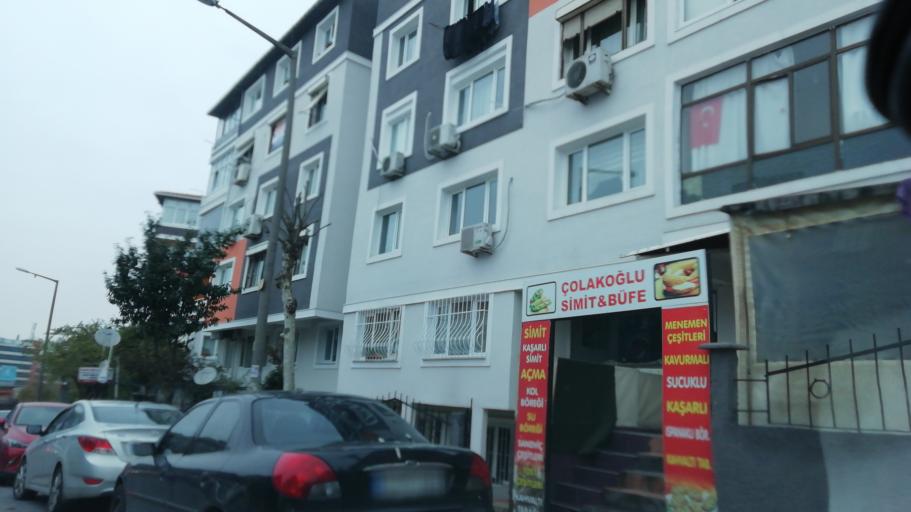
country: TR
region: Istanbul
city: Mahmutbey
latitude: 41.0177
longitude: 28.8225
